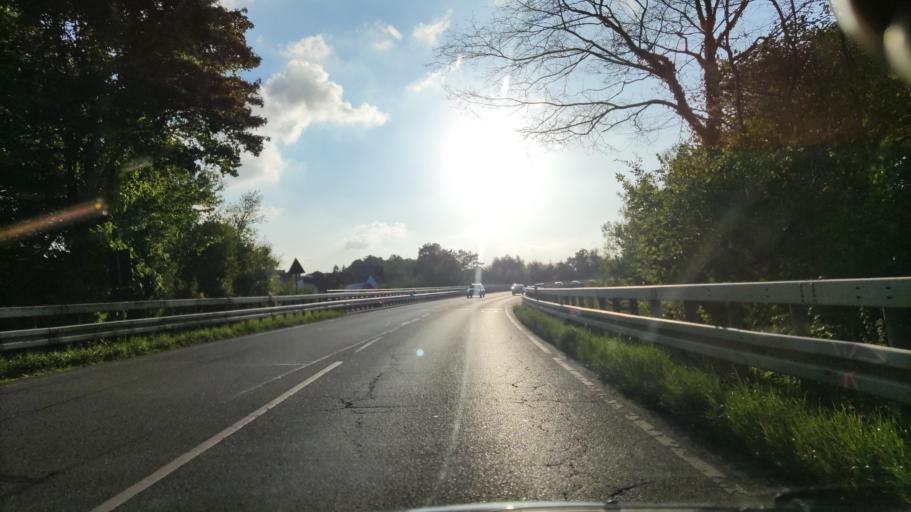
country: DE
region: Schleswig-Holstein
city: Ploen
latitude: 54.1601
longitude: 10.4119
